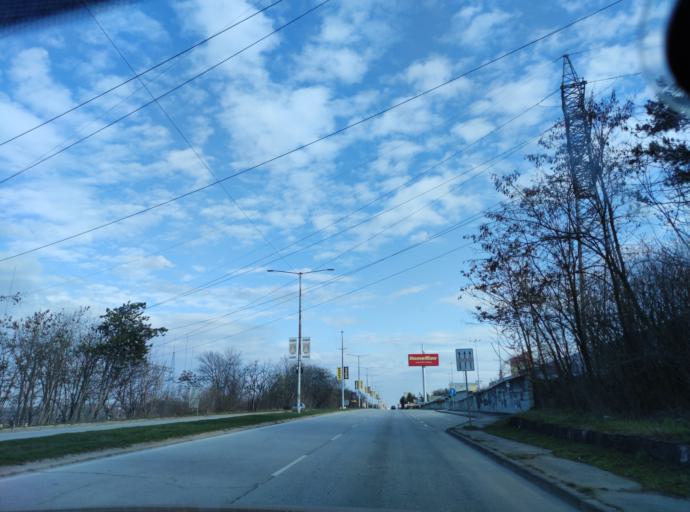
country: BG
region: Pleven
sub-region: Obshtina Pleven
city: Pleven
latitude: 43.4334
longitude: 24.5768
